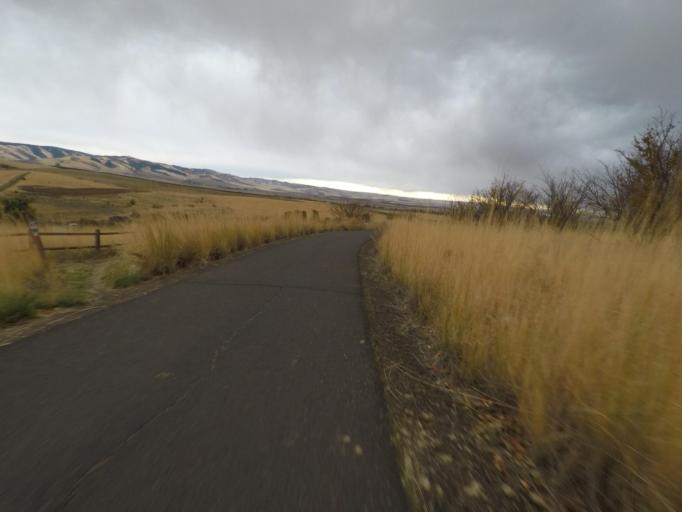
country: US
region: Washington
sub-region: Walla Walla County
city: Walla Walla East
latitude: 46.0640
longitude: -118.2669
